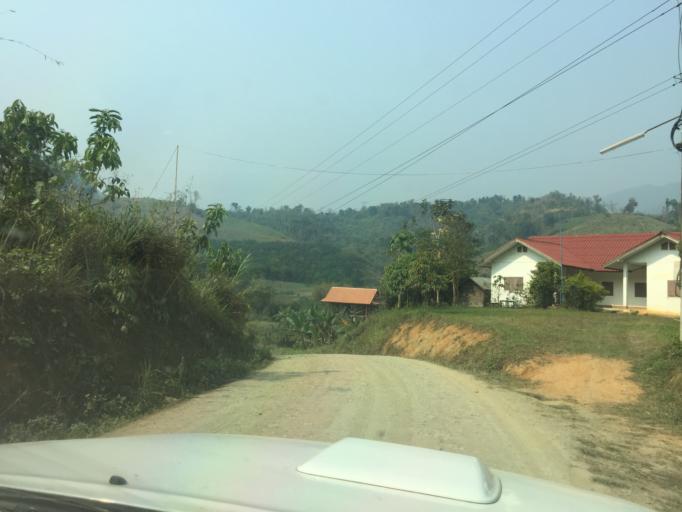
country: TH
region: Phayao
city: Phu Sang
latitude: 19.6170
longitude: 100.5366
